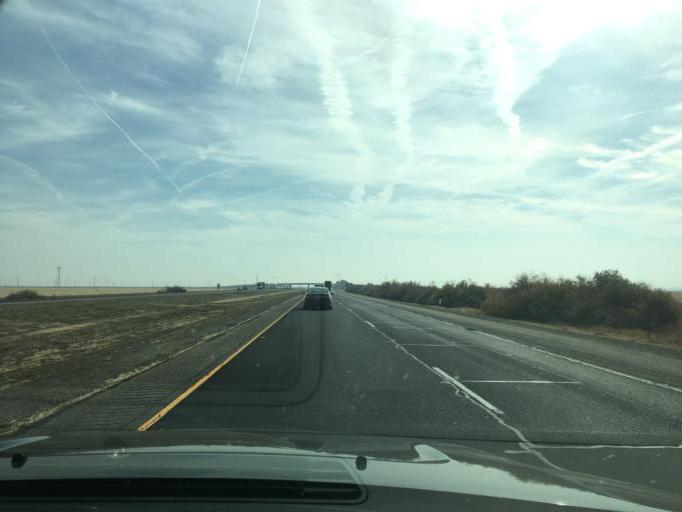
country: US
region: California
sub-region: Kern County
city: Lost Hills
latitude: 35.7389
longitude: -119.7447
